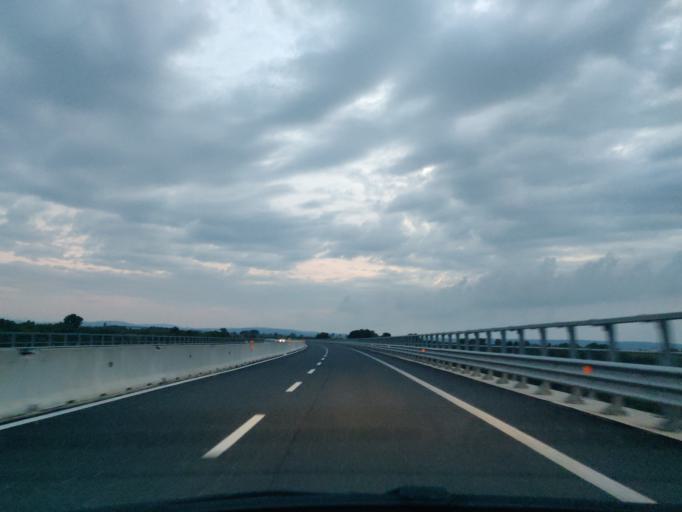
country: IT
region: Latium
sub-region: Provincia di Viterbo
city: Vetralla
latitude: 42.3596
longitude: 11.9880
